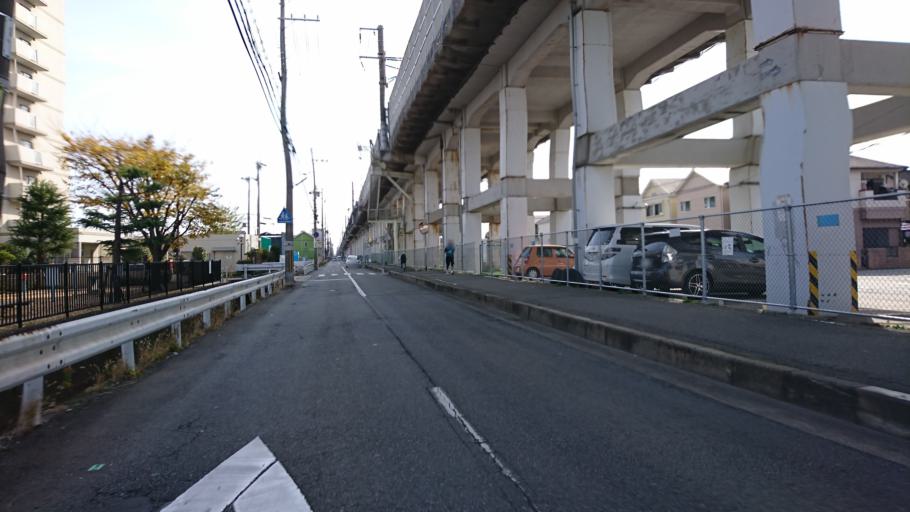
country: JP
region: Hyogo
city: Kakogawacho-honmachi
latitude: 34.7440
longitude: 134.8315
